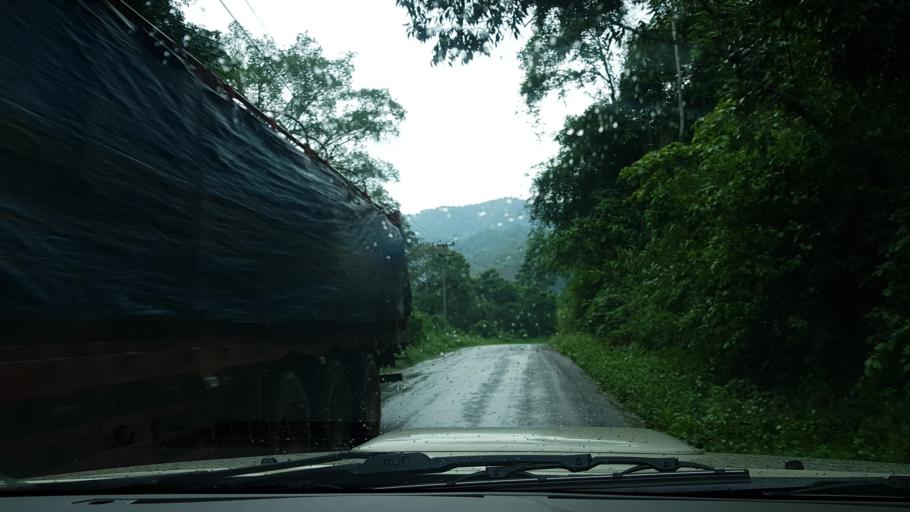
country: LA
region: Oudomxai
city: Muang Xay
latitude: 20.5996
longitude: 101.9417
